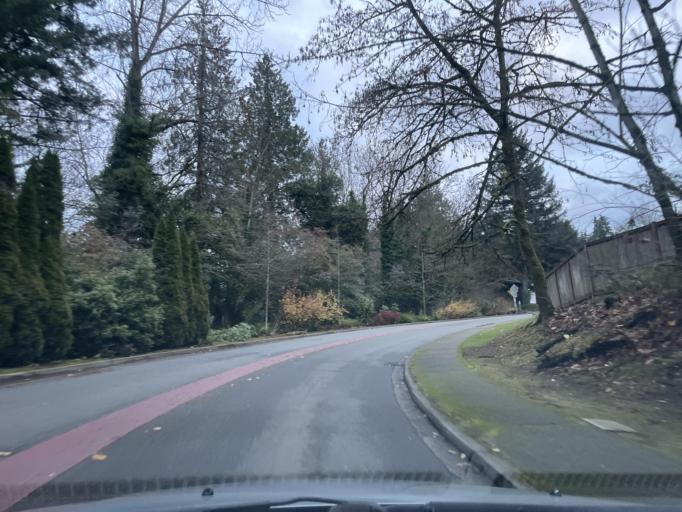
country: US
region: Washington
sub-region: King County
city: Bellevue
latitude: 47.6021
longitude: -122.1791
